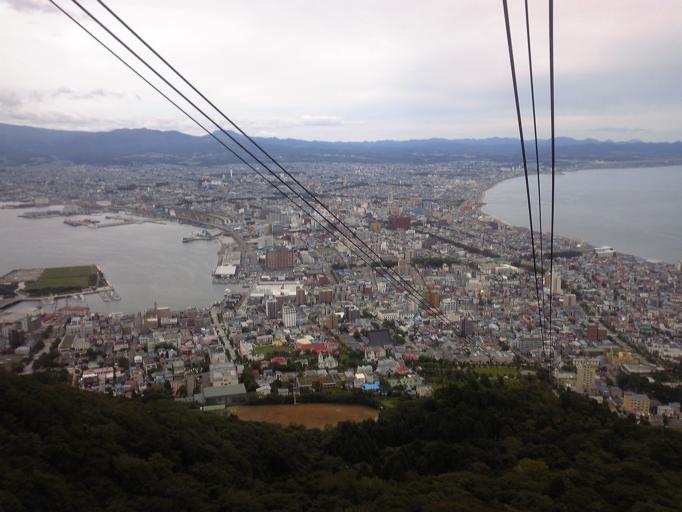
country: JP
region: Hokkaido
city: Hakodate
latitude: 41.7596
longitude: 140.7066
